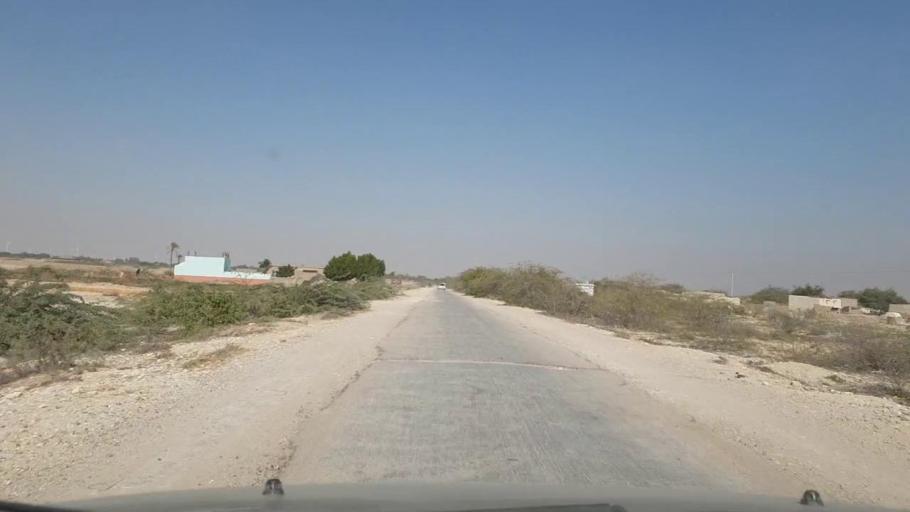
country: PK
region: Sindh
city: Daro Mehar
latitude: 25.0077
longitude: 68.0143
